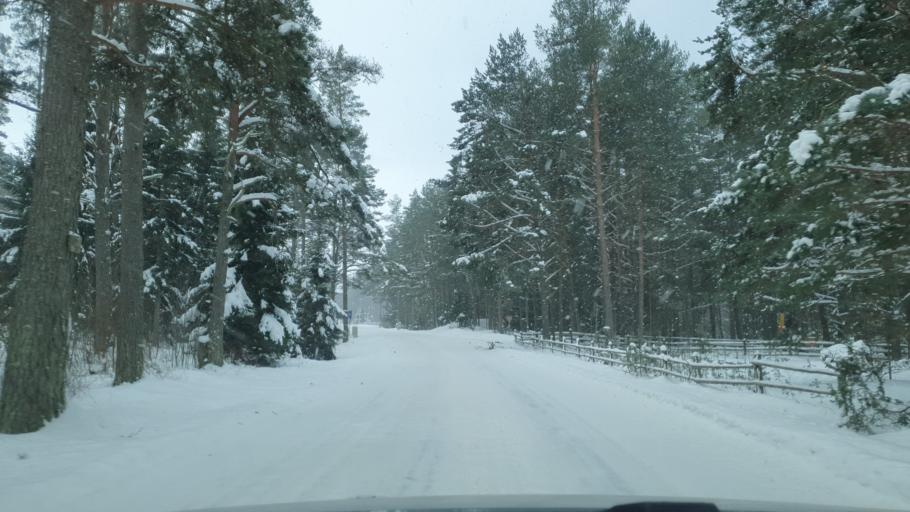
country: EE
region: Harju
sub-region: Kuusalu vald
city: Kuusalu
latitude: 59.4923
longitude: 25.3674
